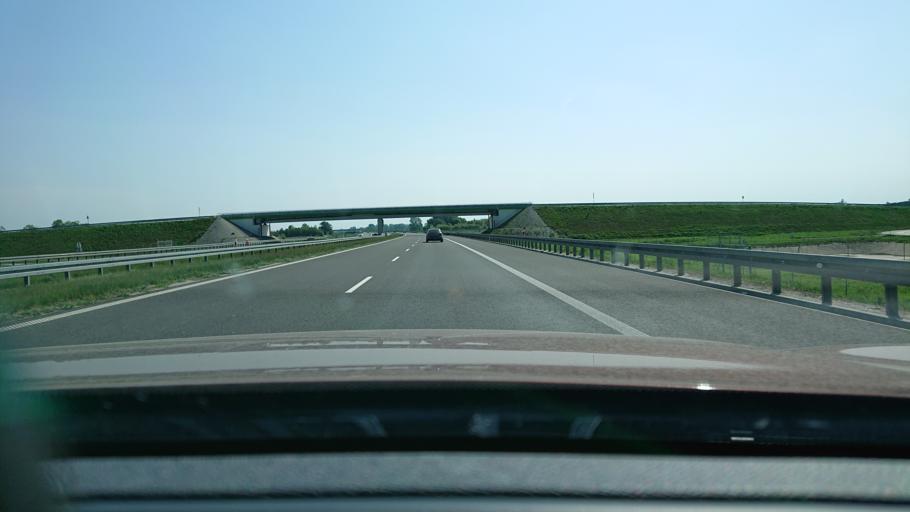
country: PL
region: Subcarpathian Voivodeship
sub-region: Powiat lancucki
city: Rogozno
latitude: 50.1109
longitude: 22.3777
